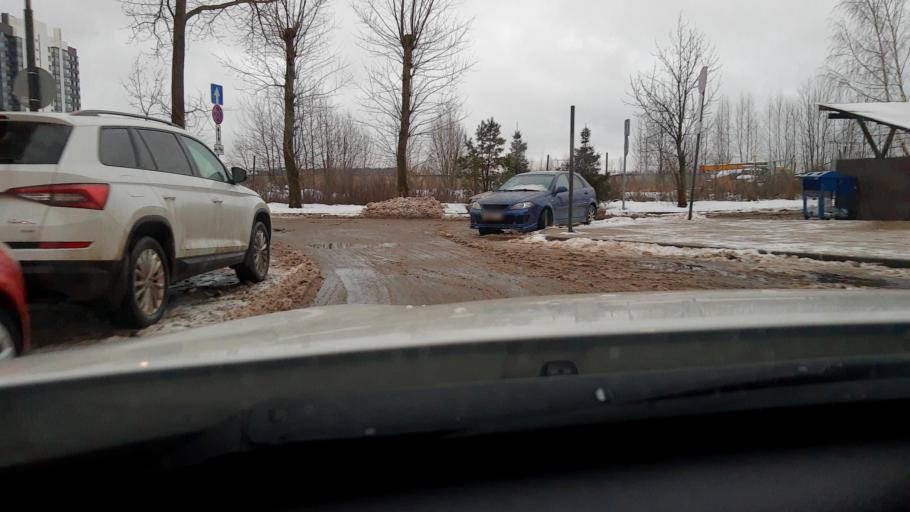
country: RU
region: Moskovskaya
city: Krasnogorsk
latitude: 55.8718
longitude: 37.3161
